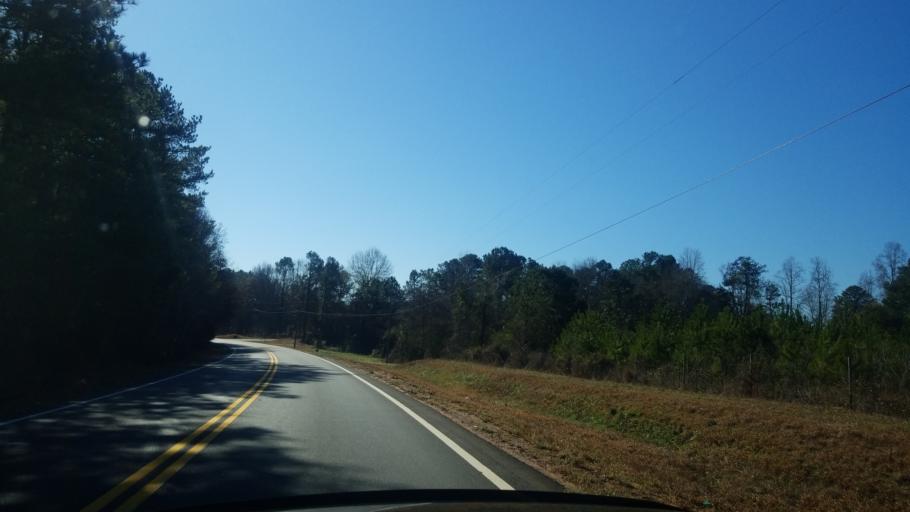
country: US
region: Alabama
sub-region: Chambers County
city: Valley
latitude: 32.8212
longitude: -85.1069
